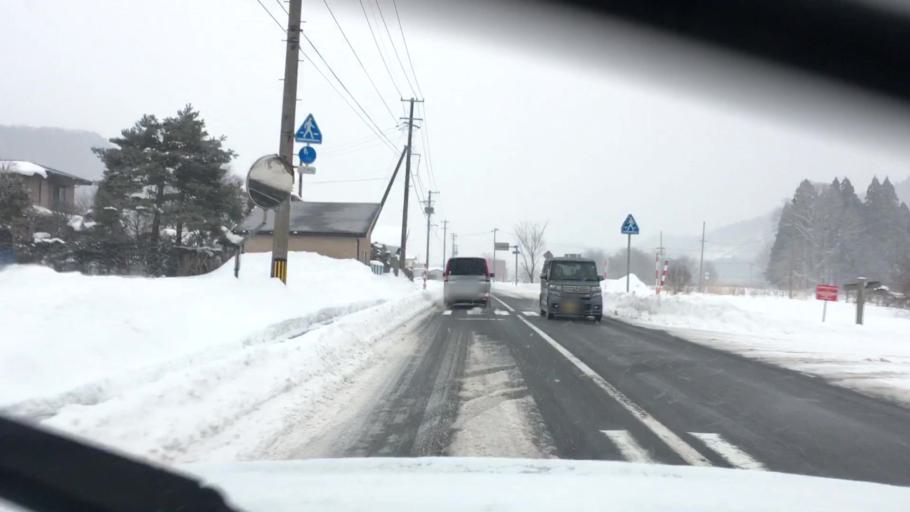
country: JP
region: Akita
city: Hanawa
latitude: 40.0879
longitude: 141.0449
